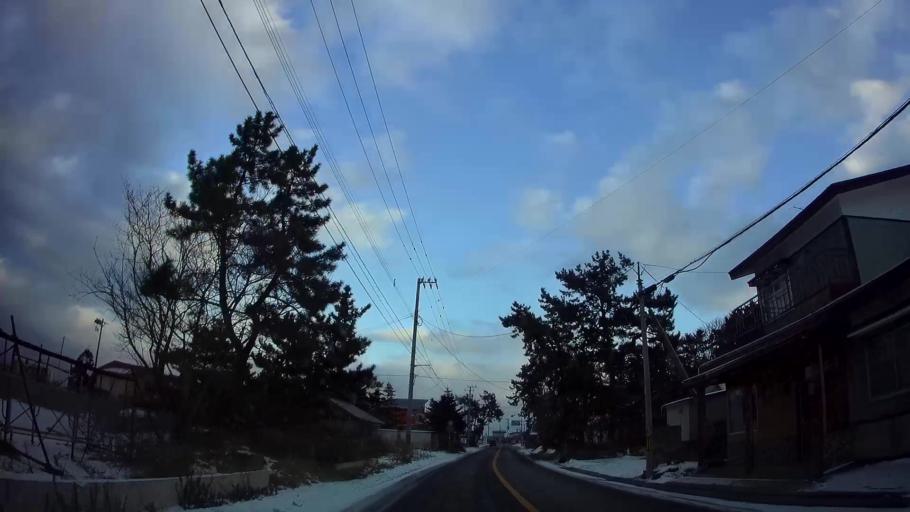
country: JP
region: Hokkaido
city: Nanae
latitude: 42.0294
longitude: 140.8285
